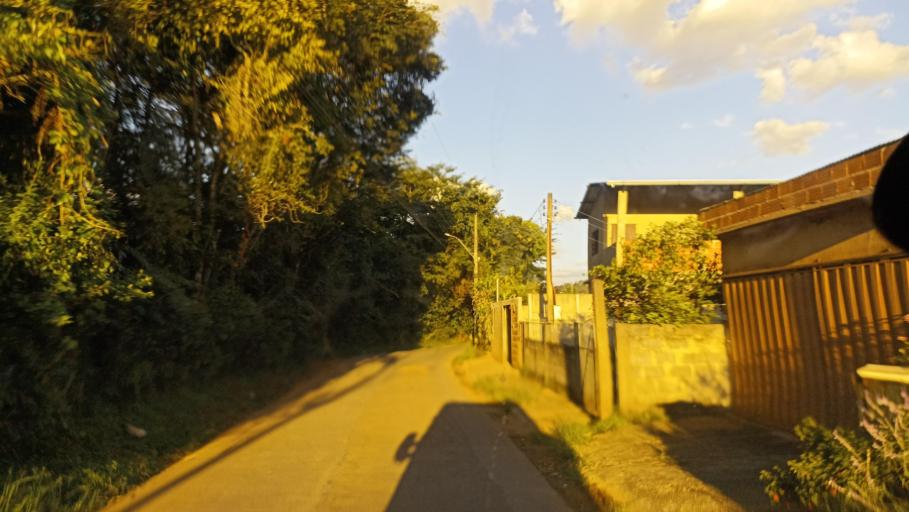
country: BR
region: Minas Gerais
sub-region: Sao Joao Del Rei
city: Sao Joao del Rei
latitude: -21.1836
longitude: -44.3342
